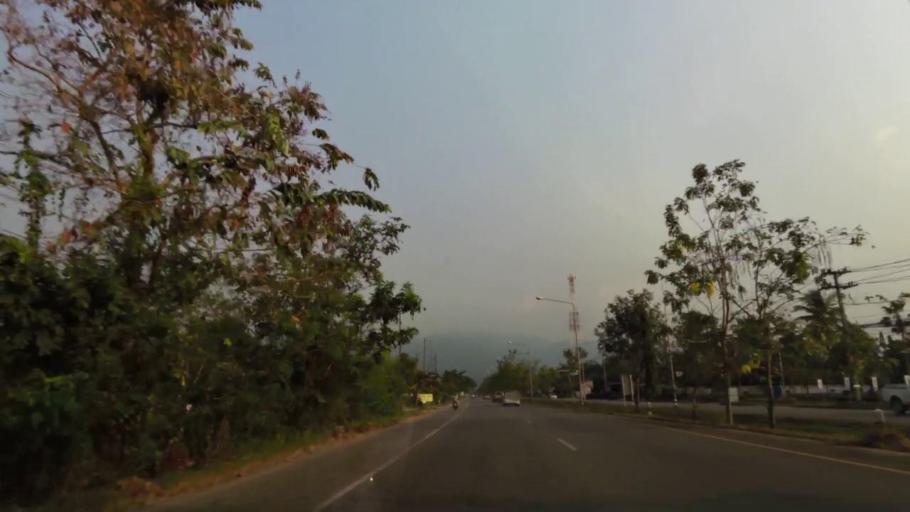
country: TH
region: Chanthaburi
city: Chanthaburi
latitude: 12.5961
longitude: 102.1431
